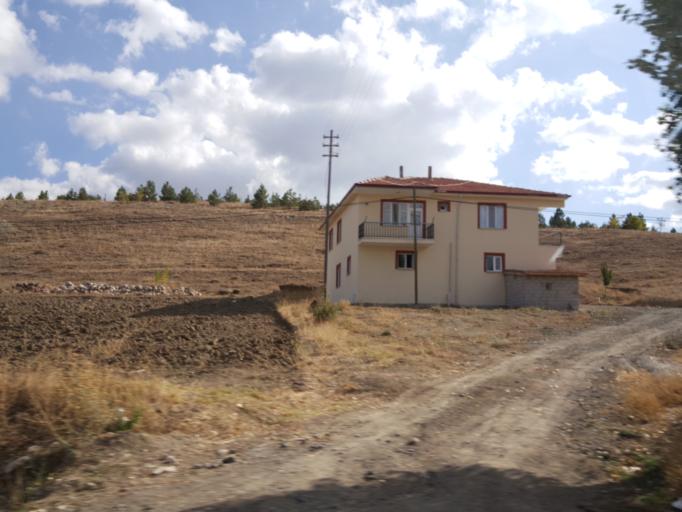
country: TR
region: Tokat
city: Sulusaray
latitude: 39.9891
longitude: 35.9964
